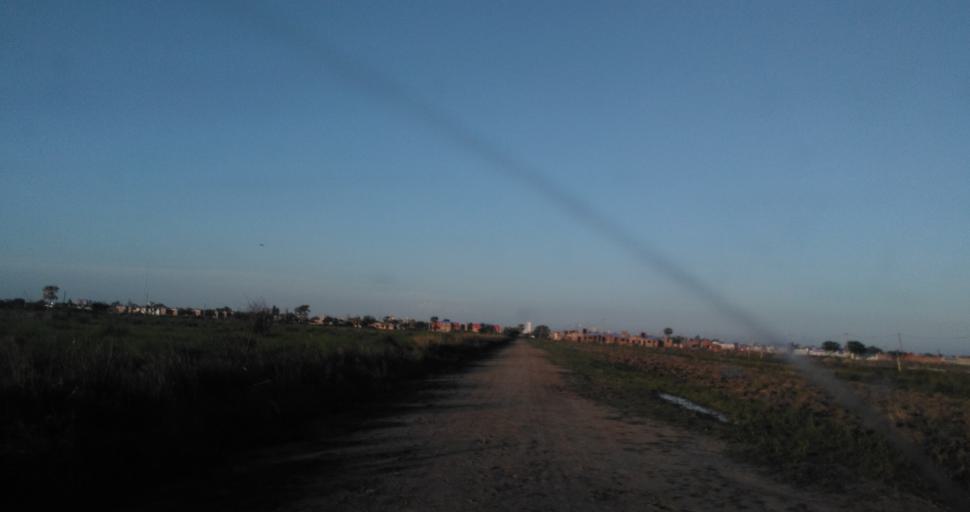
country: AR
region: Chaco
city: Resistencia
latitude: -27.4858
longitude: -59.0164
